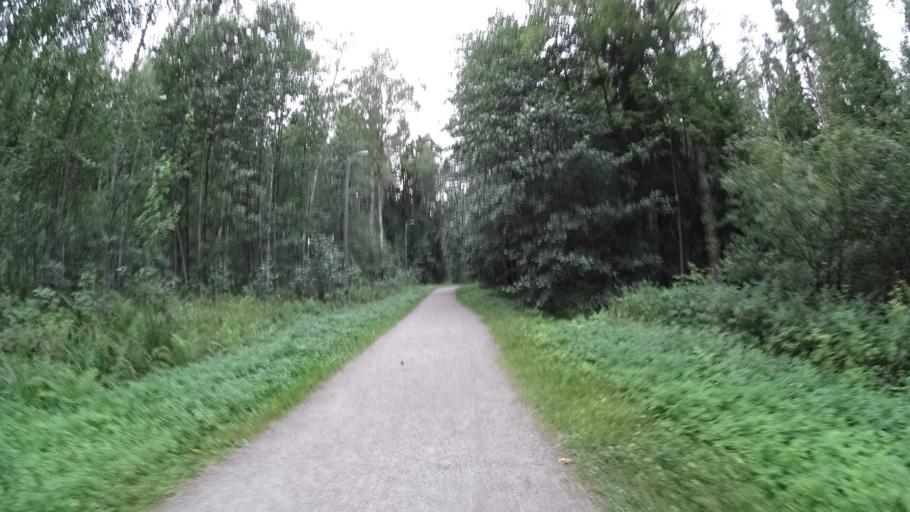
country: FI
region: Uusimaa
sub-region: Helsinki
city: Kilo
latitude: 60.2662
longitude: 24.8369
